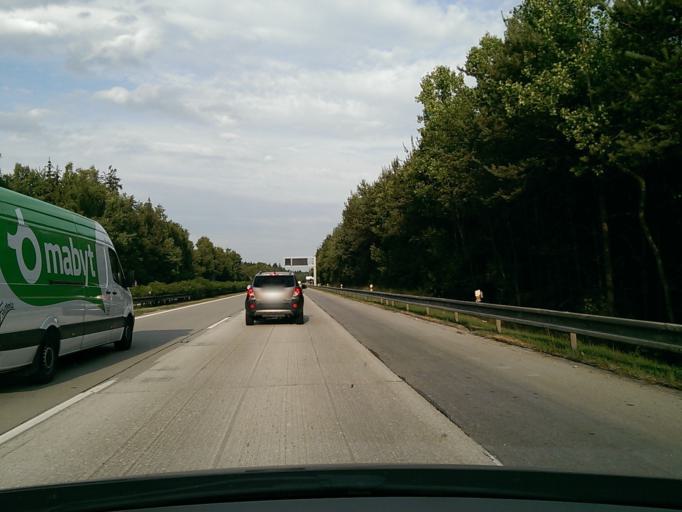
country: CZ
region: Vysocina
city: Luka nad Jihlavou
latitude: 49.4117
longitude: 15.7249
